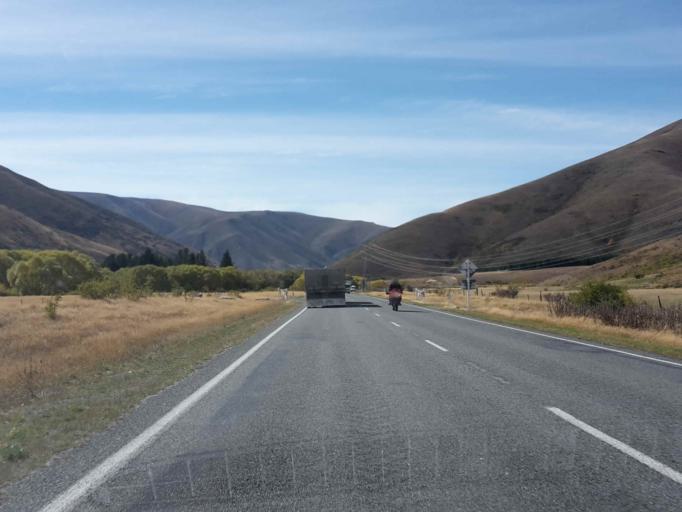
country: NZ
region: Otago
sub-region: Queenstown-Lakes District
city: Wanaka
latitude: -44.5275
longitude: 169.7166
